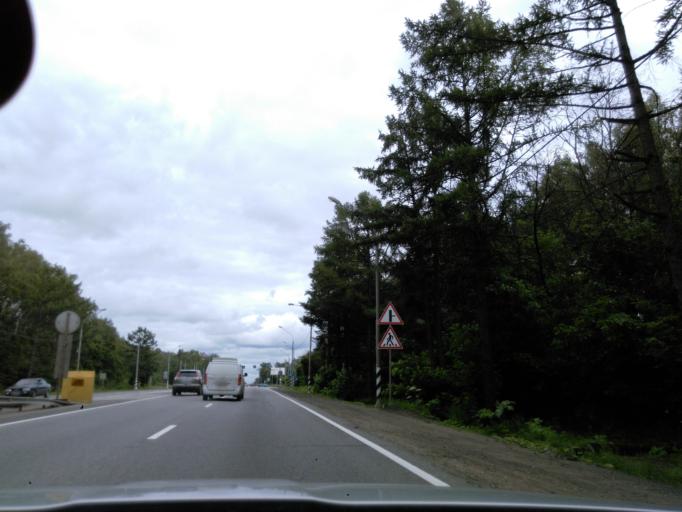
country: RU
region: Moskovskaya
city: Chashnikovo
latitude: 56.0249
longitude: 37.1805
